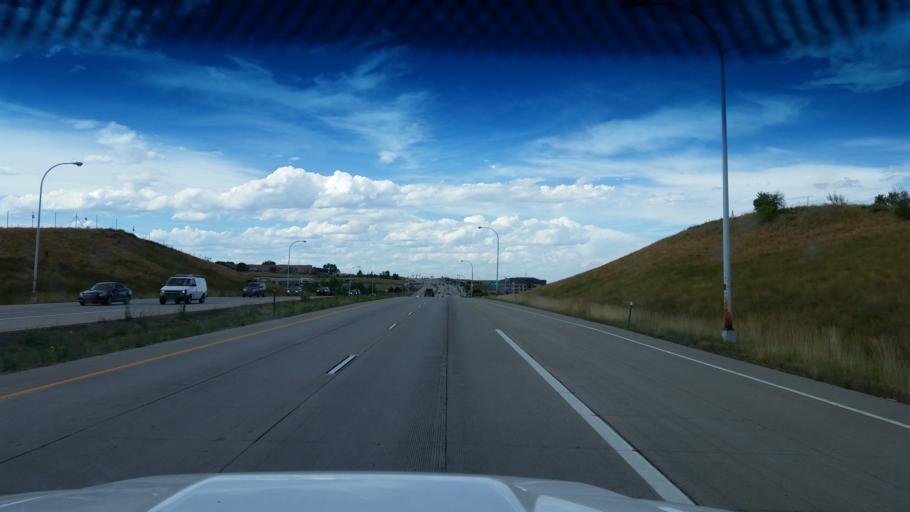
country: US
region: Colorado
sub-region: Broomfield County
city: Broomfield
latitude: 39.9000
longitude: -105.0959
